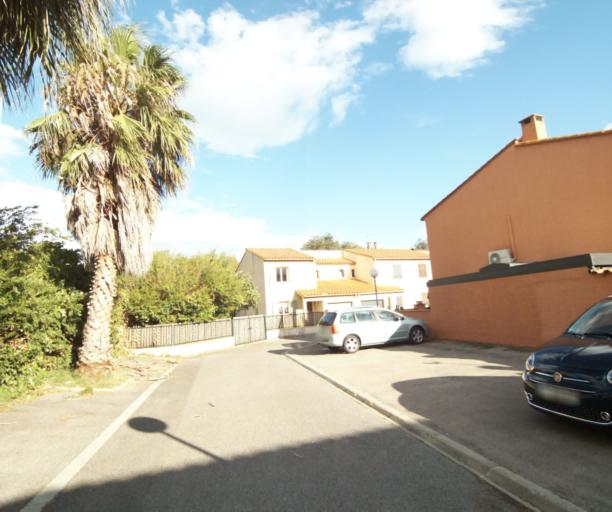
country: FR
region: Languedoc-Roussillon
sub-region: Departement des Pyrenees-Orientales
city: Argelers
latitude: 42.5508
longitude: 3.0395
